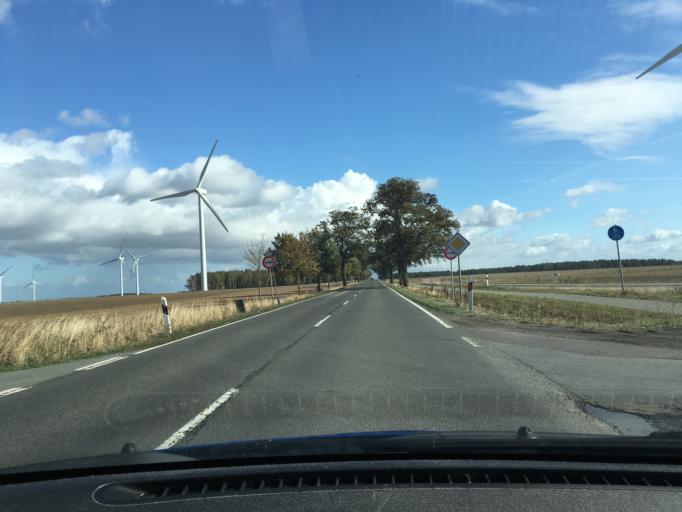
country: DE
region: Saxony-Anhalt
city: Pretzier
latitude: 52.8391
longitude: 11.2221
